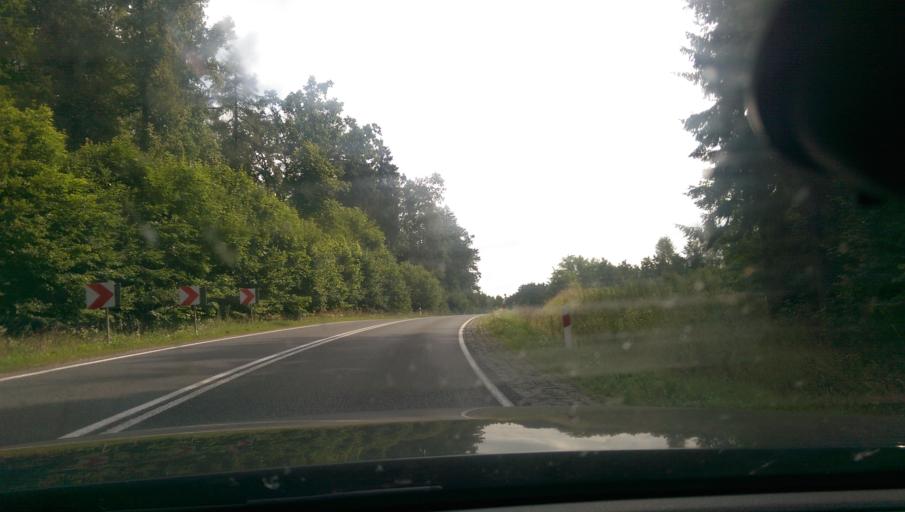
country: PL
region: Warmian-Masurian Voivodeship
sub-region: Powiat gizycki
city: Gizycko
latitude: 54.0623
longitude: 21.7974
